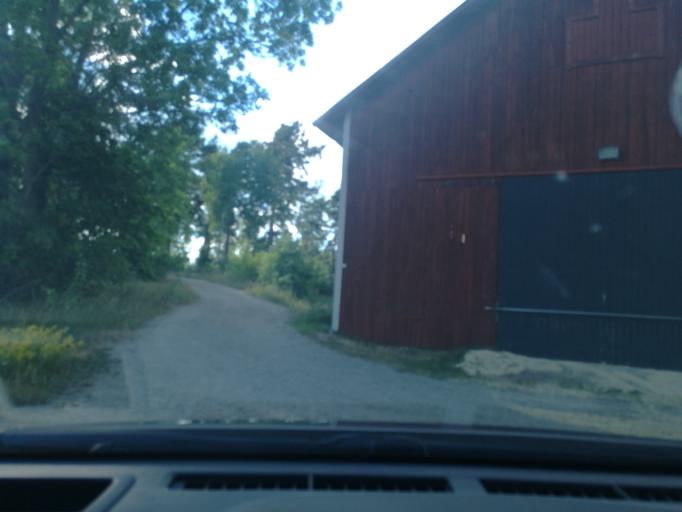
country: SE
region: Soedermanland
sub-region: Eskilstuna Kommun
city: Arla
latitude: 59.3821
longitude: 16.6857
